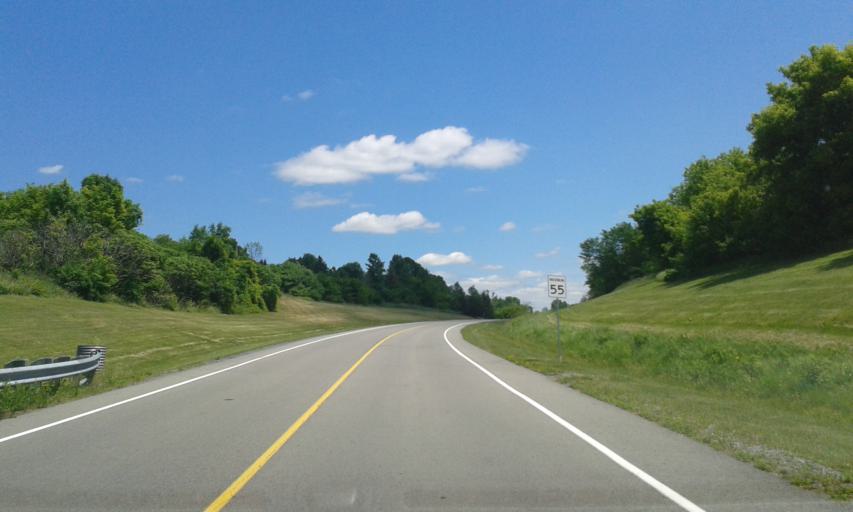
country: US
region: New York
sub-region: St. Lawrence County
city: Massena
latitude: 44.9952
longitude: -74.9254
